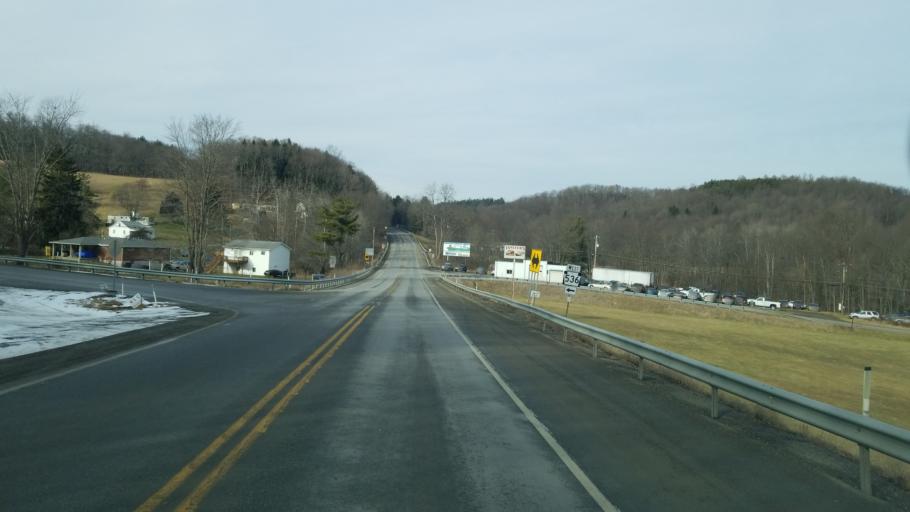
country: US
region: Pennsylvania
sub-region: Jefferson County
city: Punxsutawney
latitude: 40.9699
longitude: -79.0127
